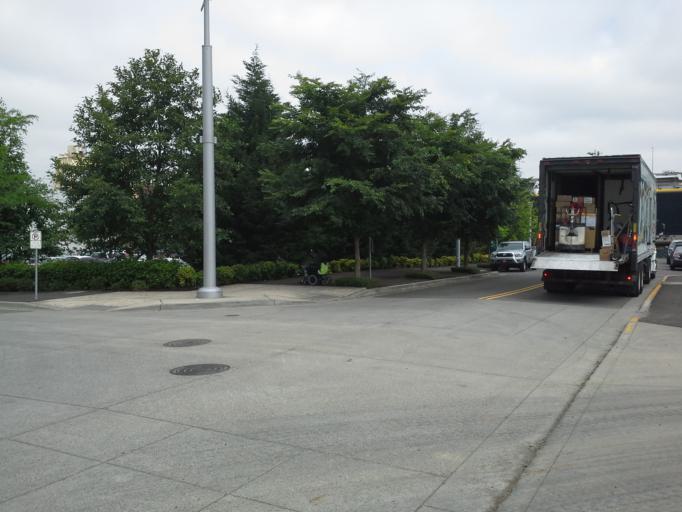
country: US
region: Oregon
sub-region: Multnomah County
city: Portland
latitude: 45.4985
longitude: -122.6696
